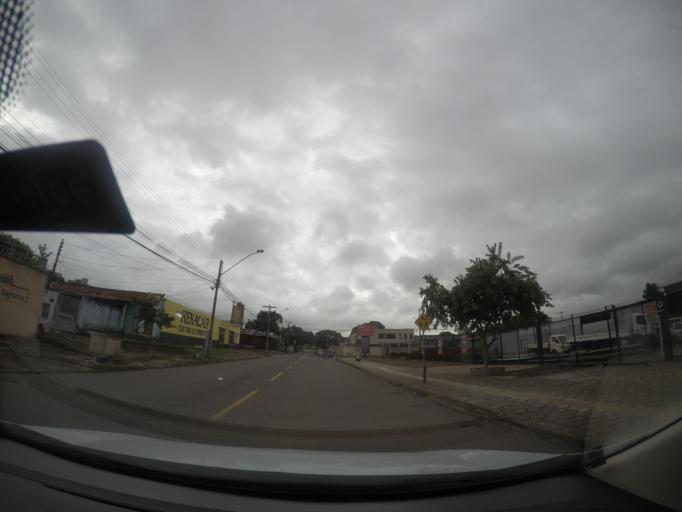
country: BR
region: Goias
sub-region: Goiania
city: Goiania
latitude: -16.7136
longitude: -49.2909
